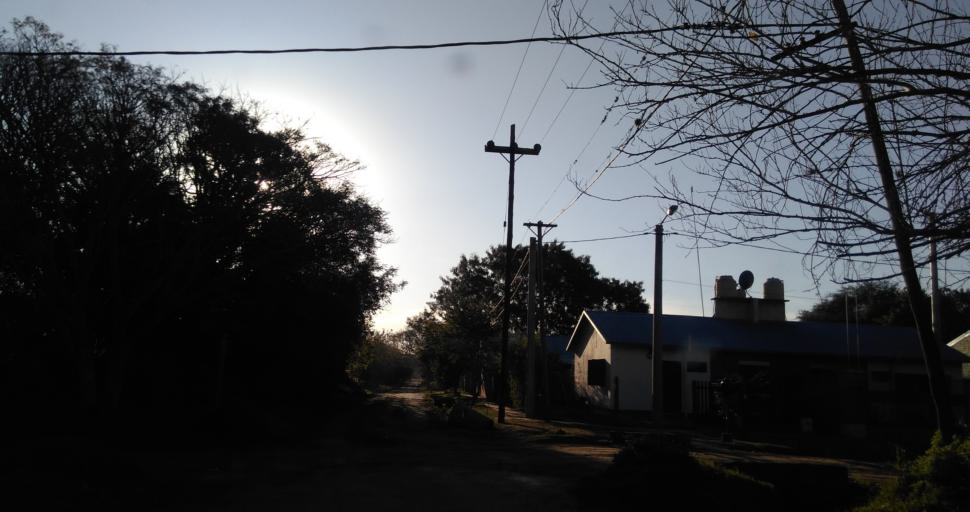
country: AR
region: Chaco
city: Colonia Benitez
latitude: -27.3314
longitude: -58.9576
